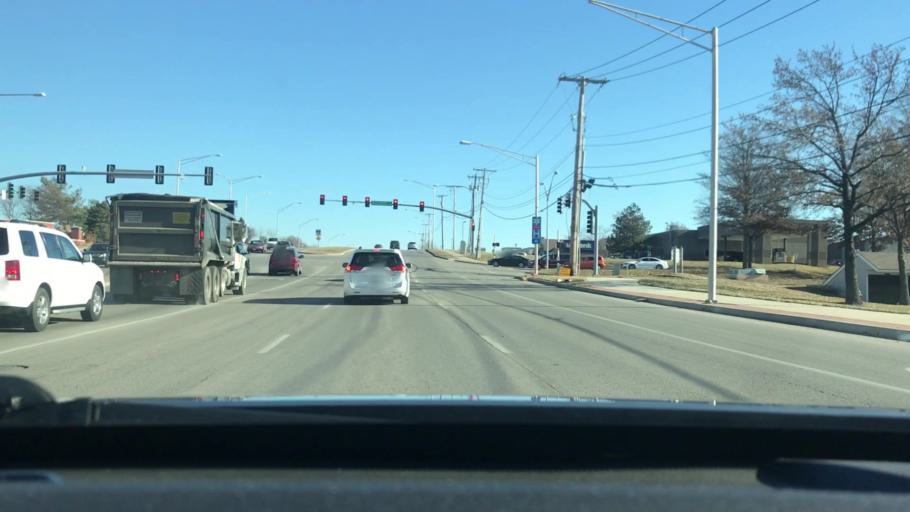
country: US
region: Missouri
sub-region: Platte County
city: Weatherby Lake
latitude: 39.2469
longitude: -94.6524
